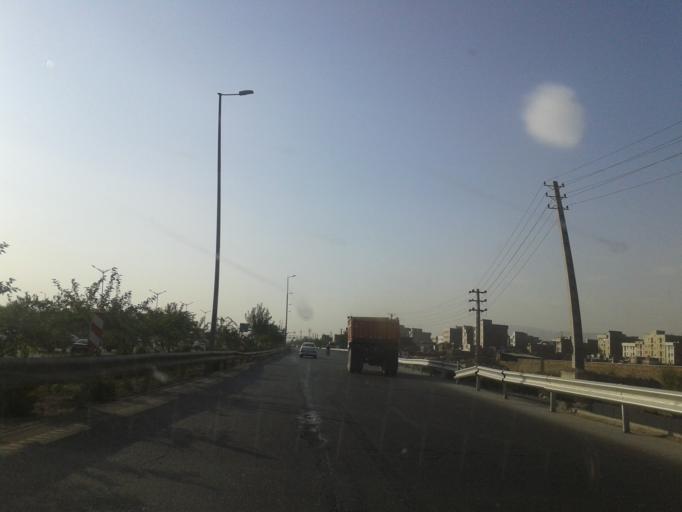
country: IR
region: Tehran
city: Eslamshahr
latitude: 35.6516
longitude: 51.2712
